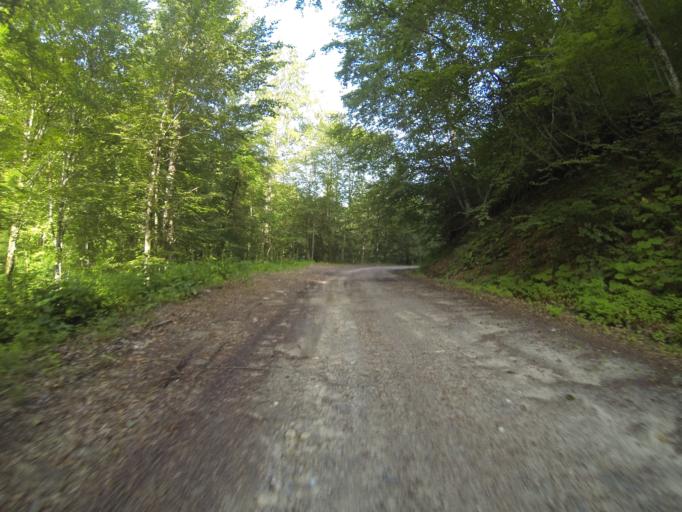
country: RO
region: Valcea
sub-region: Oras Baile Olanesti
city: Baile Olanesti
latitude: 45.2402
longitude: 24.1904
